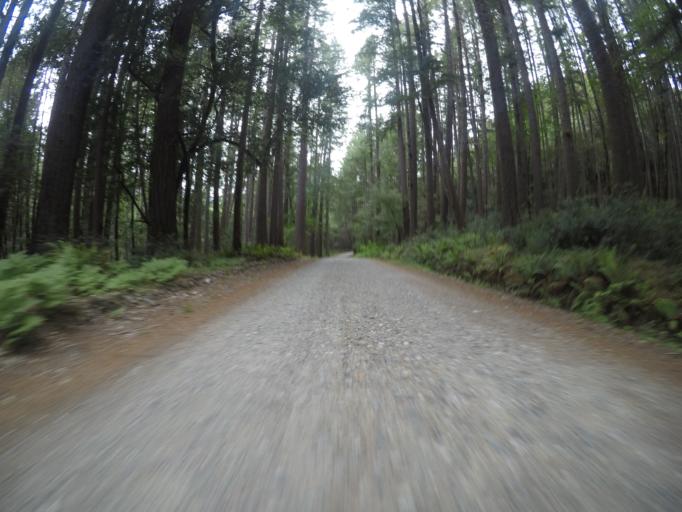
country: US
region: California
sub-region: Del Norte County
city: Bertsch-Oceanview
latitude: 41.7017
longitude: -123.8986
